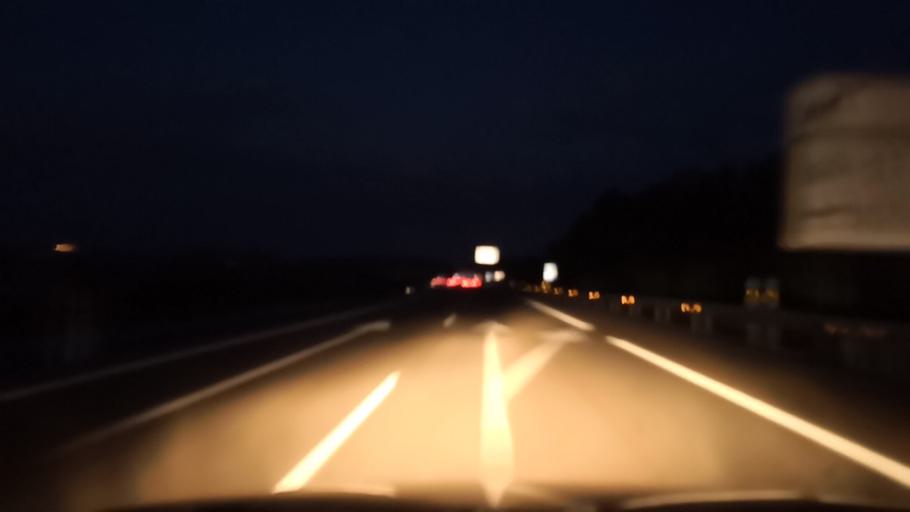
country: ES
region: Castille and Leon
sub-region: Provincia de Leon
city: Brazuelo
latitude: 42.5357
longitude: -6.1529
